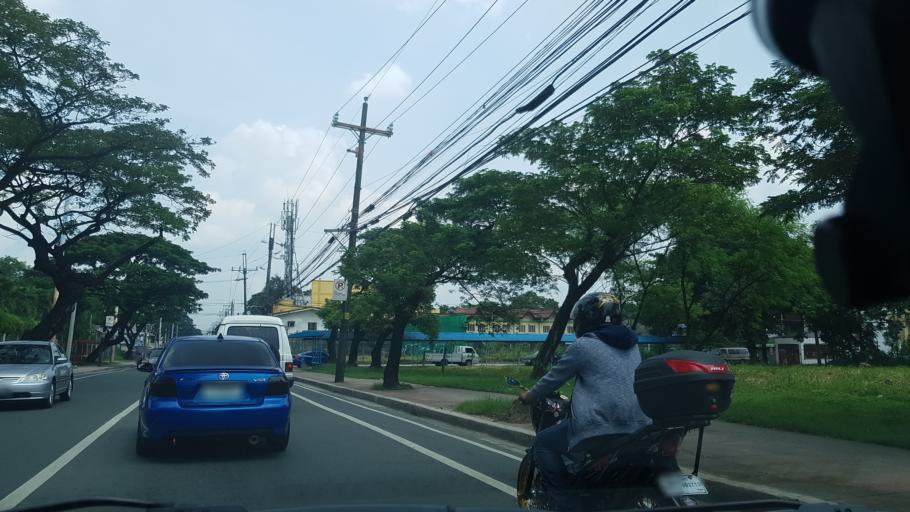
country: PH
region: Calabarzon
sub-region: Province of Rizal
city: San Mateo
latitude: 14.6666
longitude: 121.1074
